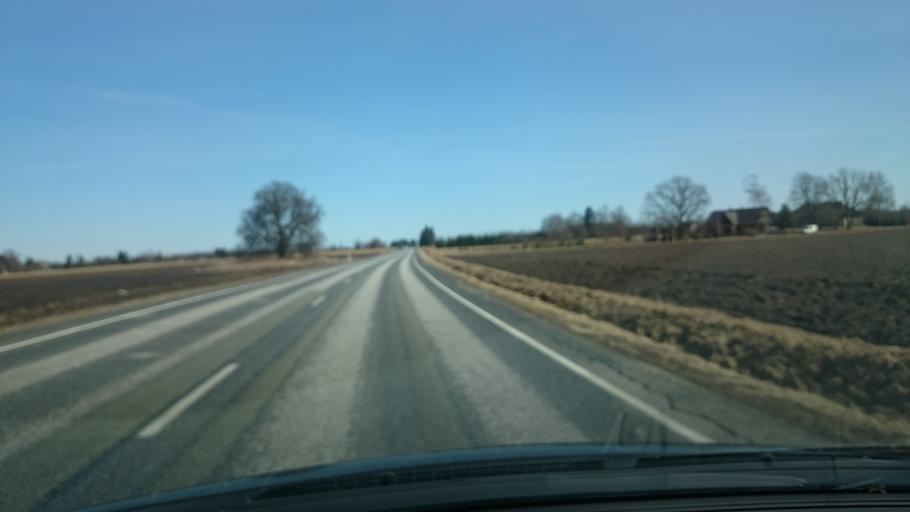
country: EE
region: Jaervamaa
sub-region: Tueri vald
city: Sarevere
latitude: 58.7544
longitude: 25.3377
